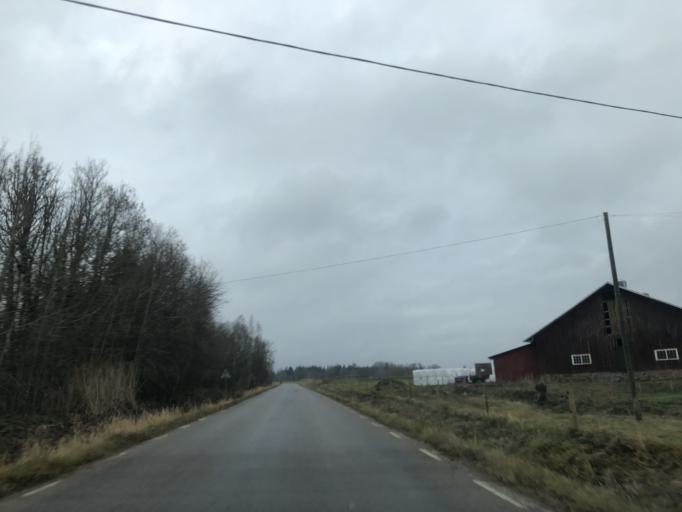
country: SE
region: Vaestra Goetaland
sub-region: Ulricehamns Kommun
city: Ulricehamn
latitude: 57.8829
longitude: 13.5148
